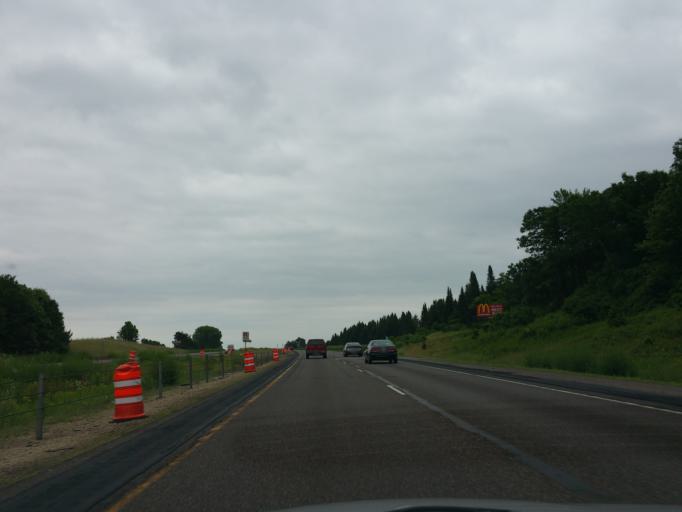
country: US
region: Wisconsin
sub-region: Eau Claire County
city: Eau Claire
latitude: 44.8529
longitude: -91.6473
